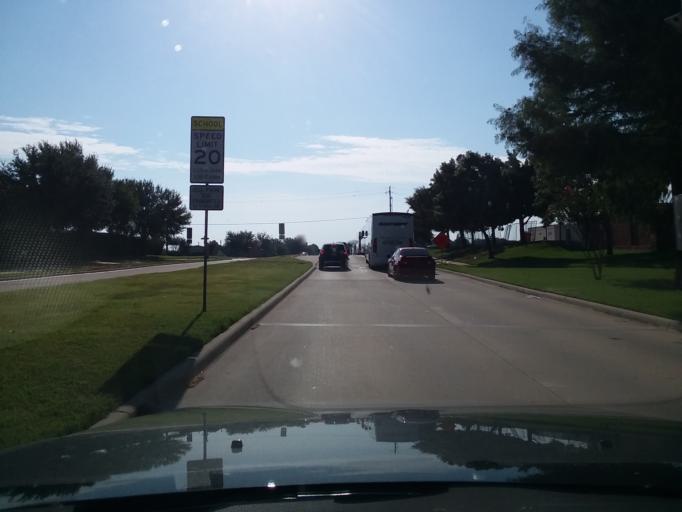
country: US
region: Texas
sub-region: Denton County
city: Highland Village
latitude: 33.0663
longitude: -97.0655
